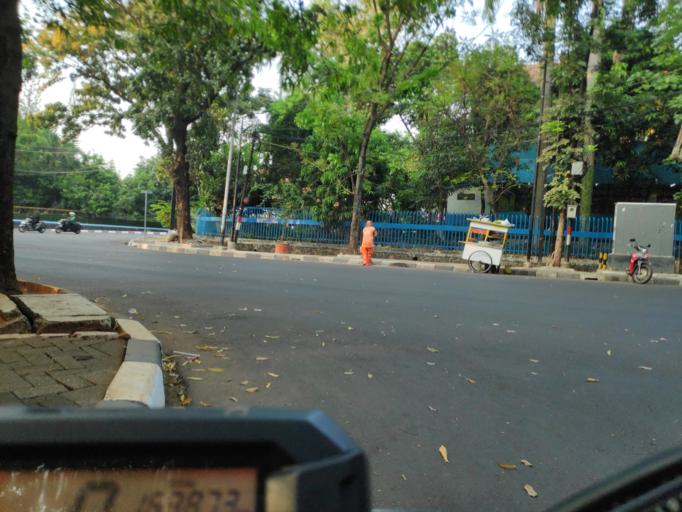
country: ID
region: Jakarta Raya
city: Jakarta
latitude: -6.2494
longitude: 106.8036
